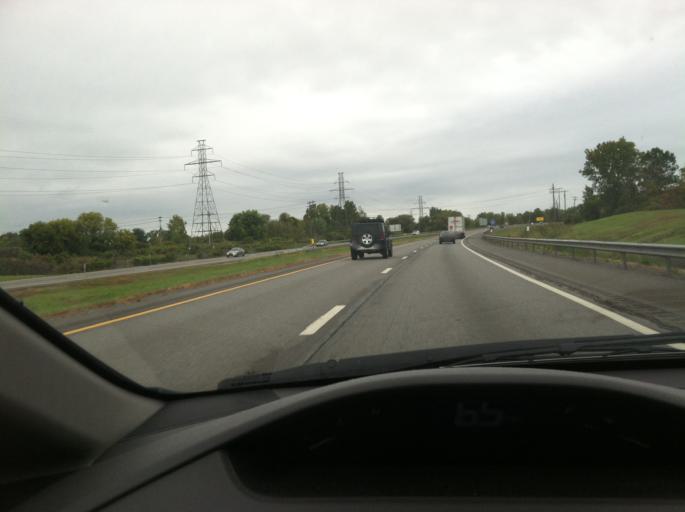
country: US
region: New York
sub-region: Erie County
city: Blasdell
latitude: 42.7926
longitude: -78.8163
